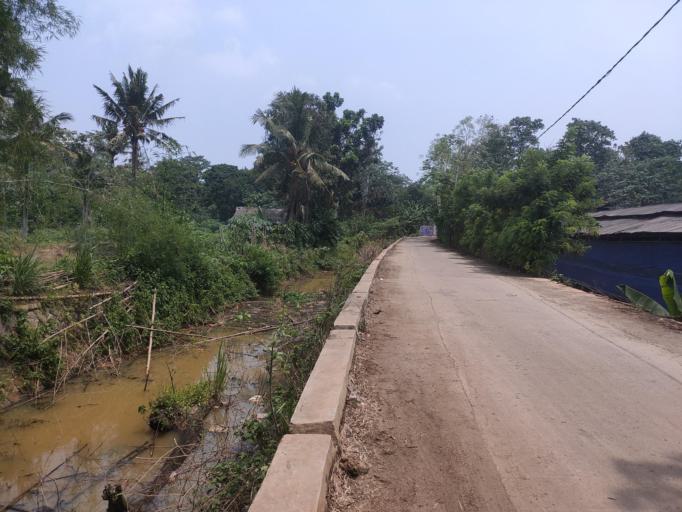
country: ID
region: West Java
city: Parung
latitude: -6.3873
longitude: 106.7237
